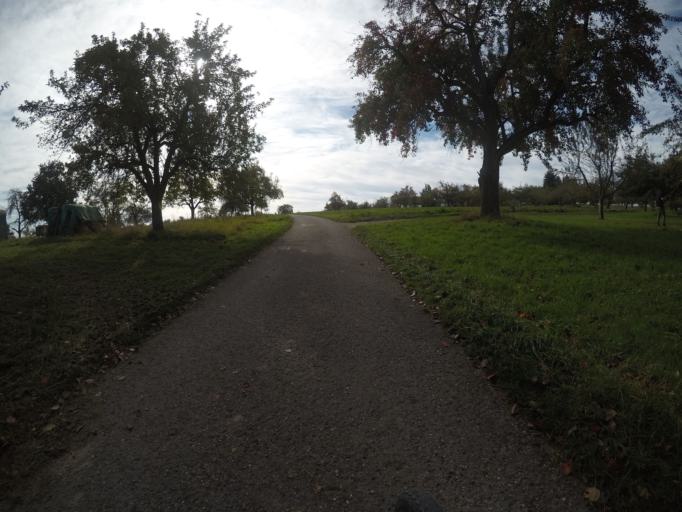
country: DE
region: Baden-Wuerttemberg
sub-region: Regierungsbezirk Stuttgart
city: Gartringen
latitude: 48.6557
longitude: 8.9057
